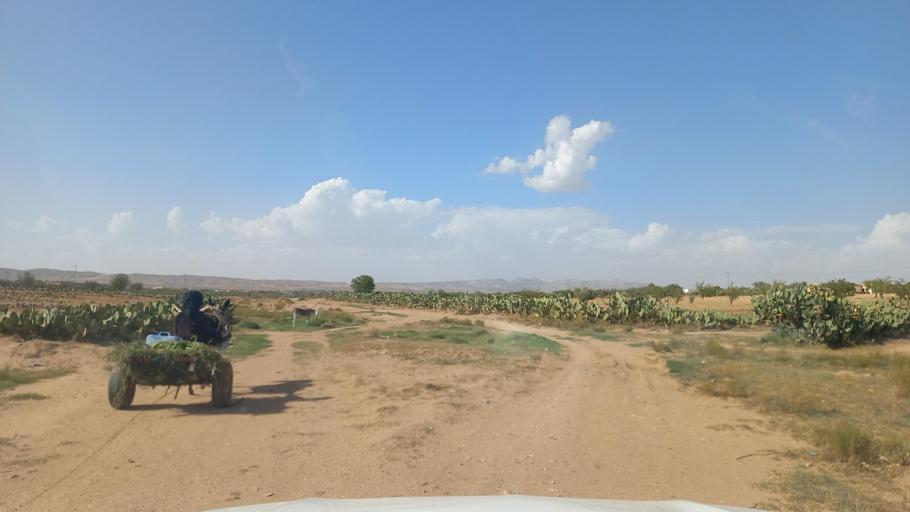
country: TN
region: Al Qasrayn
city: Sbiba
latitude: 35.3097
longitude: 9.0336
